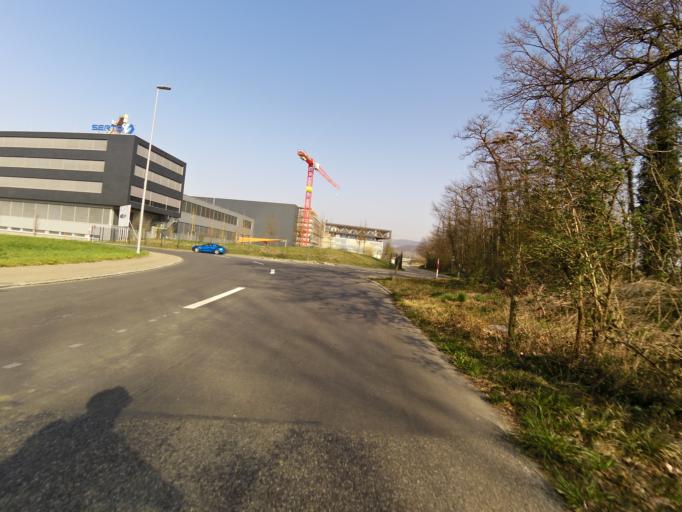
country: CH
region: Thurgau
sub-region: Frauenfeld District
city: Frauenfeld
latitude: 47.5735
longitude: 8.9206
